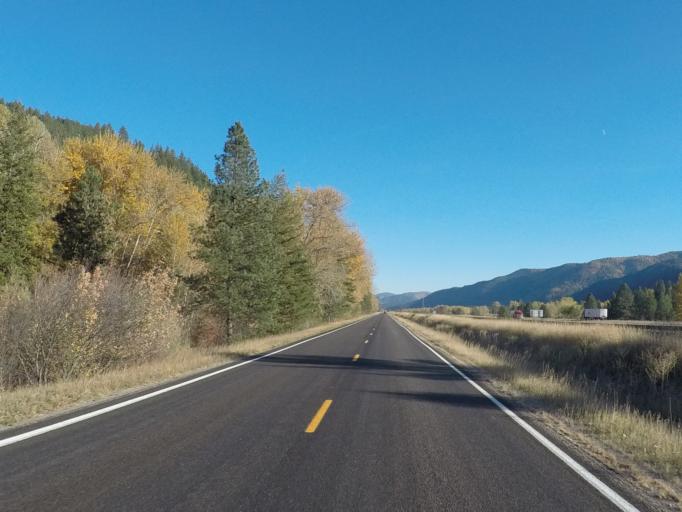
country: US
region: Montana
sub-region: Missoula County
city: Bonner-West Riverside
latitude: 46.8281
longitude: -113.8130
